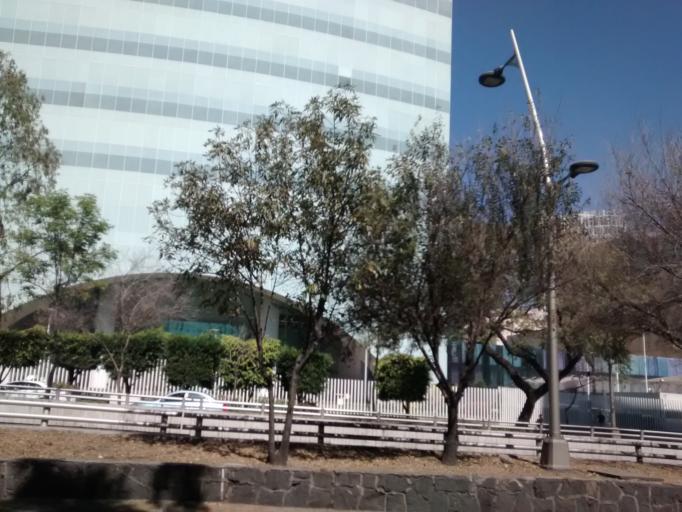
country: MX
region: Mexico City
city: Miguel Hidalgo
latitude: 19.4383
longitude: -99.2049
